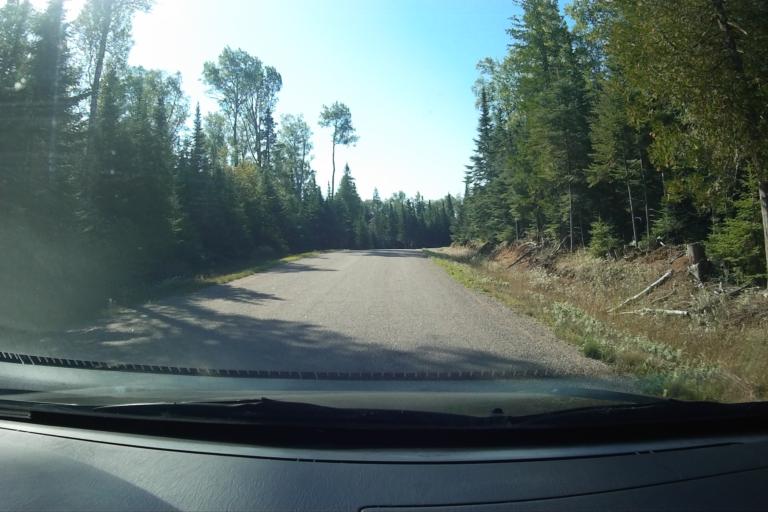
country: CA
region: Ontario
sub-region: Thunder Bay District
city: Thunder Bay
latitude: 48.3493
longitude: -88.8063
